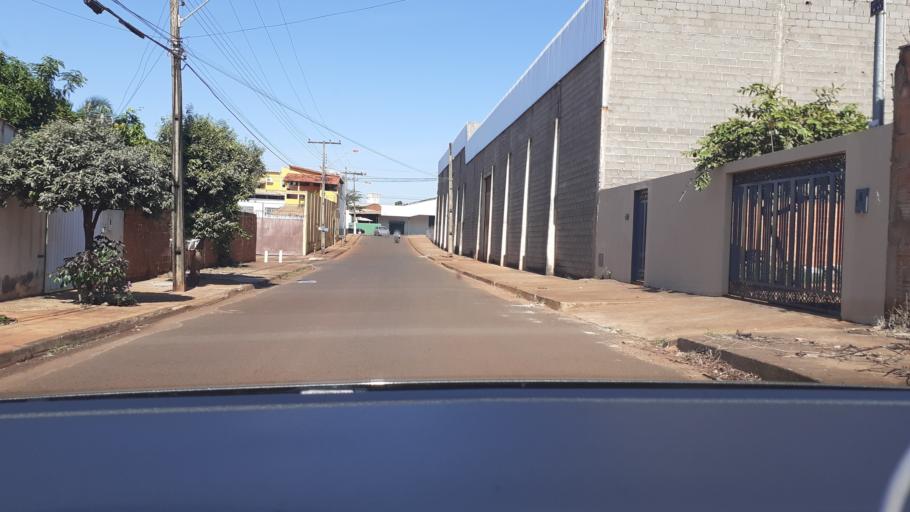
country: BR
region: Goias
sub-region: Itumbiara
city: Itumbiara
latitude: -18.4081
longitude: -49.2530
